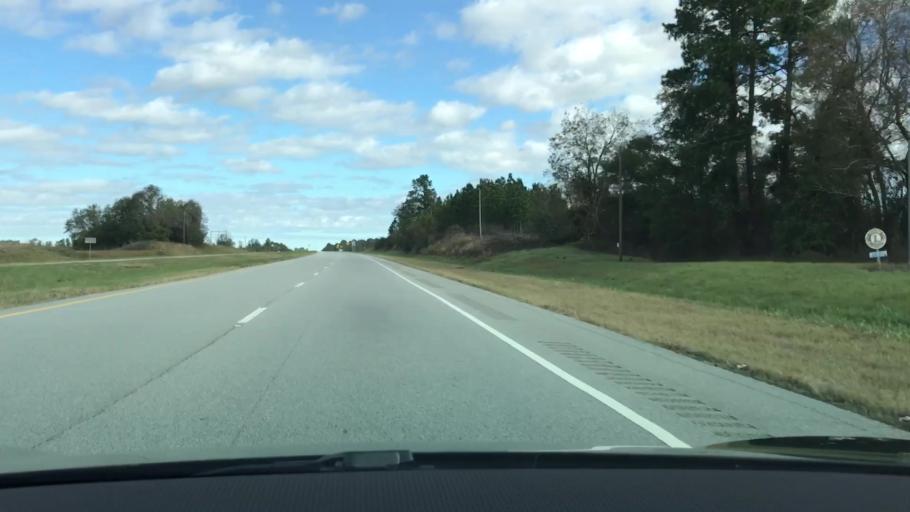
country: US
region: Georgia
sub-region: Jefferson County
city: Wadley
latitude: 32.8388
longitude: -82.3995
